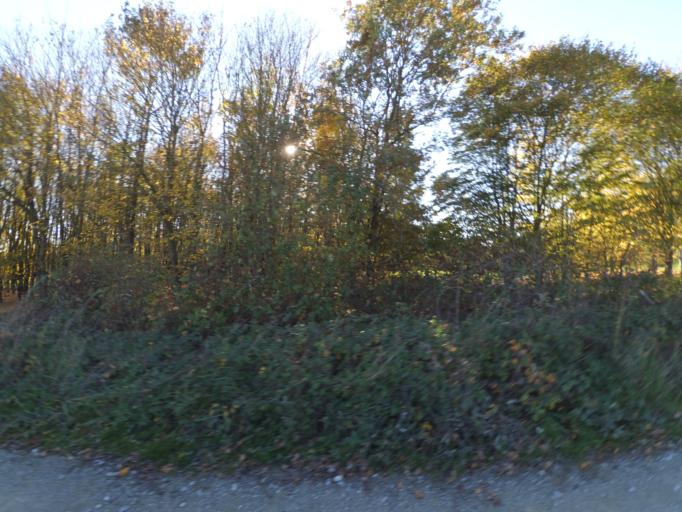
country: FR
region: Pays de la Loire
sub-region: Departement de la Loire-Atlantique
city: La Planche
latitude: 47.0216
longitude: -1.3962
